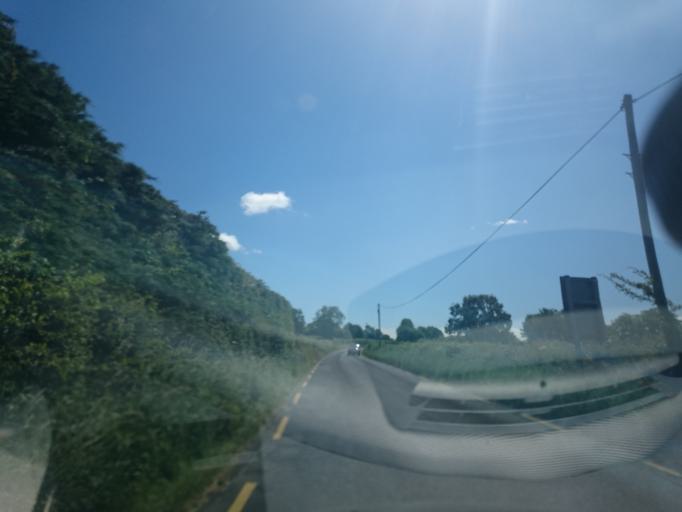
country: IE
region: Leinster
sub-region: Kilkenny
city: Graiguenamanagh
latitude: 52.5988
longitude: -6.9915
